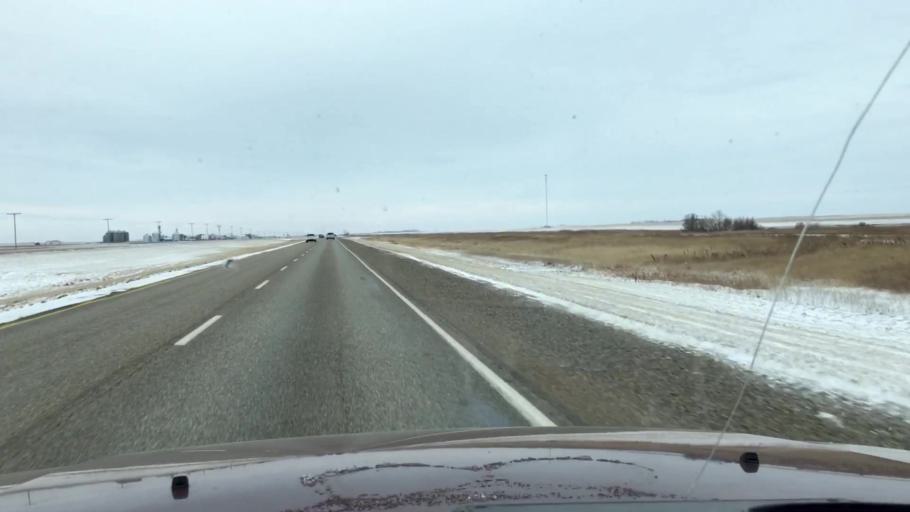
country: CA
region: Saskatchewan
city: Moose Jaw
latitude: 51.0201
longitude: -105.7862
